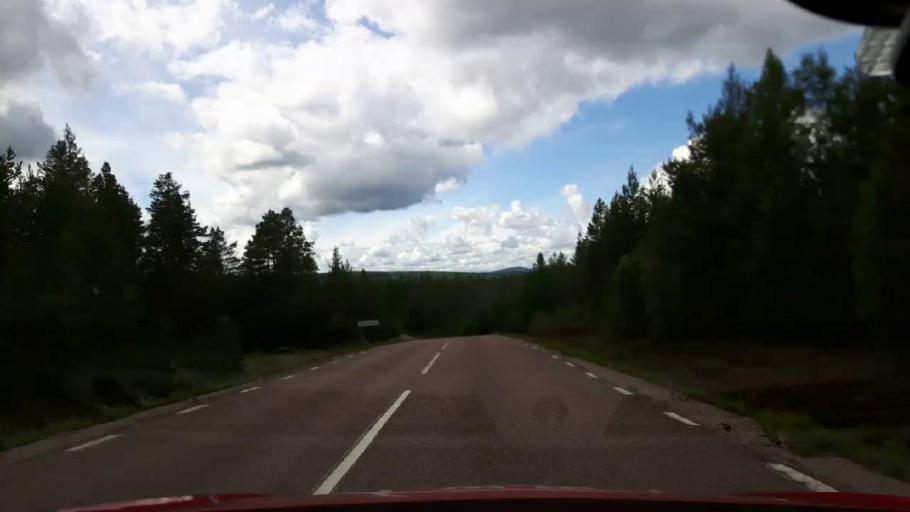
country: SE
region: Jaemtland
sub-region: Harjedalens Kommun
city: Sveg
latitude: 61.8254
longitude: 13.8666
